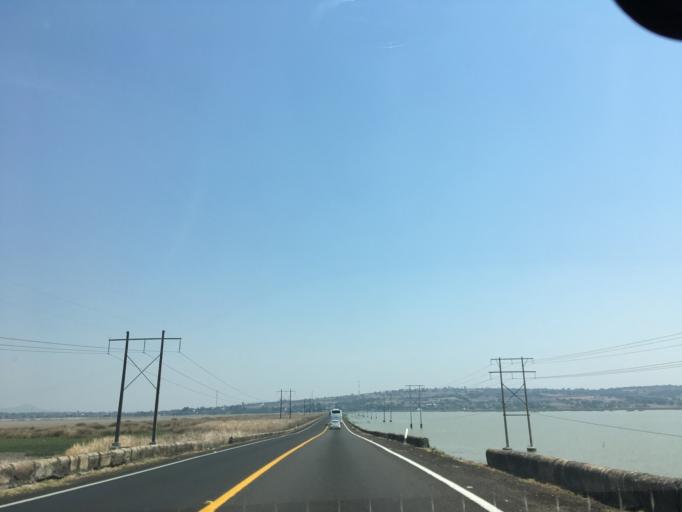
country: MX
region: Michoacan
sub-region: Cuitzeo
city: San Juan Benito Juarez (San Juan Tararameo)
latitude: 19.9418
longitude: -101.1380
